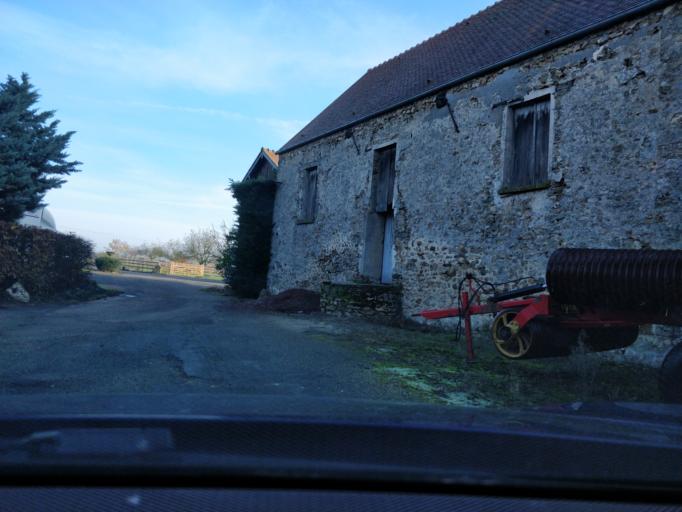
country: FR
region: Ile-de-France
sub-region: Departement de l'Essonne
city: Limours
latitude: 48.6509
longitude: 2.0916
